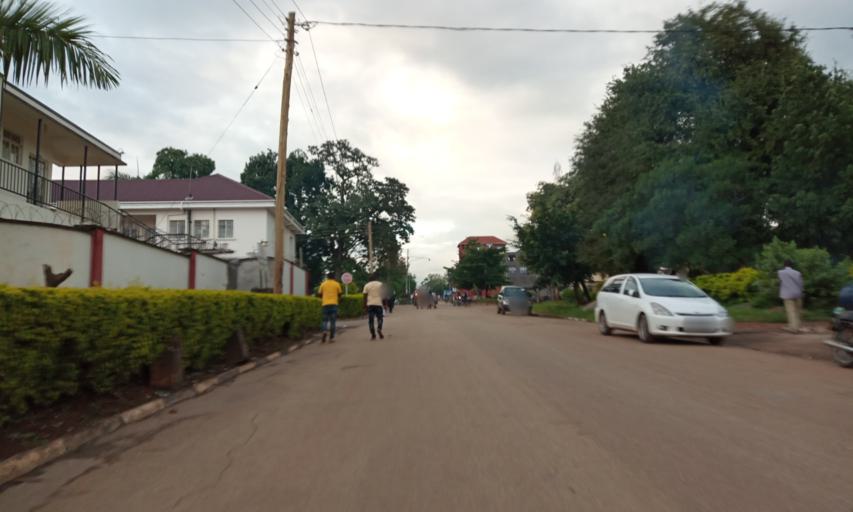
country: UG
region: Eastern Region
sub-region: Mbale District
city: Mbale
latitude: 1.0690
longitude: 34.1806
